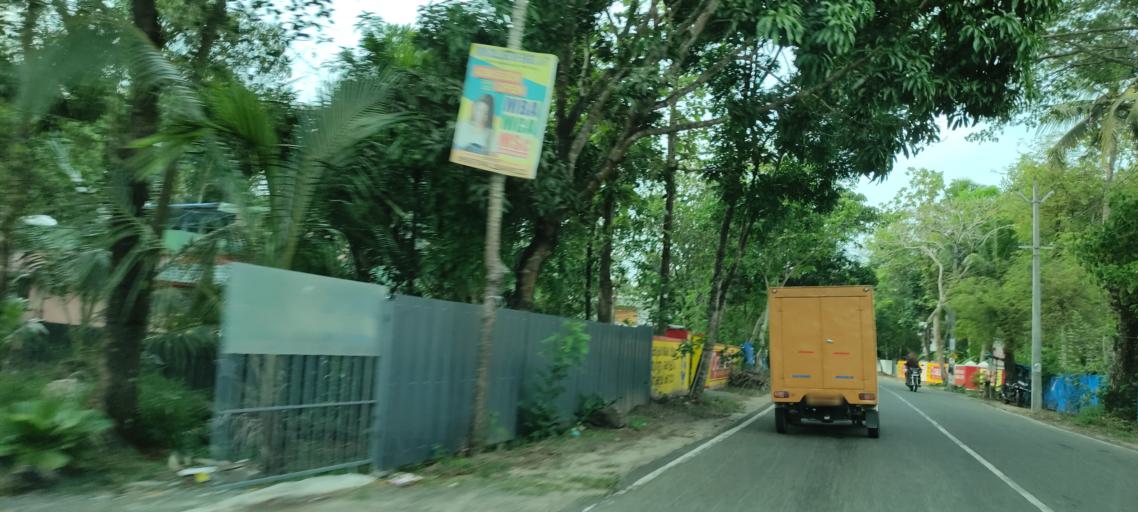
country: IN
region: Kerala
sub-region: Kottayam
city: Vaikam
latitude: 9.7584
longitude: 76.3626
